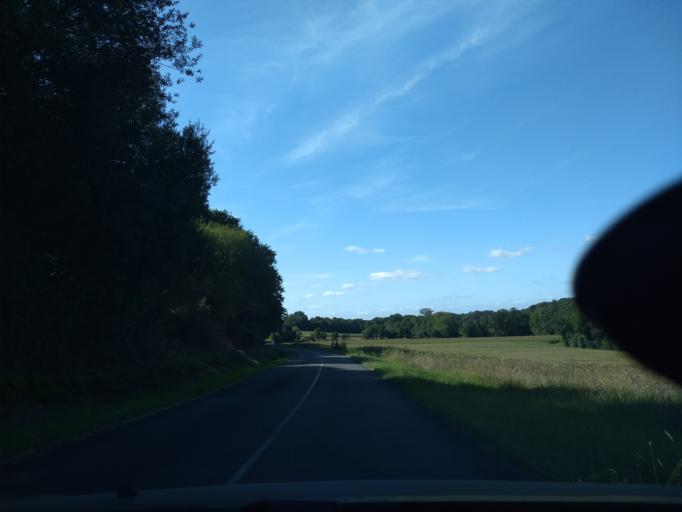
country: FR
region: Aquitaine
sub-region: Departement des Pyrenees-Atlantiques
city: Soumoulou
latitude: 43.2926
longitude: -0.1507
